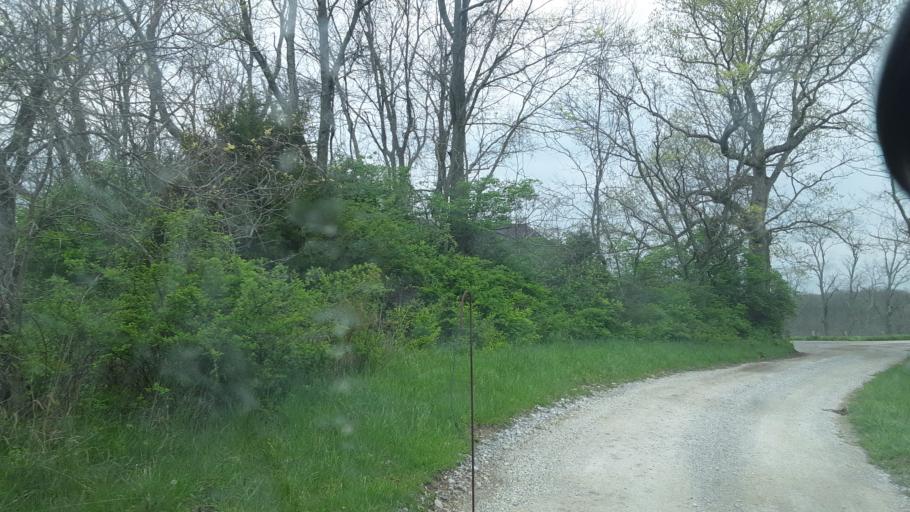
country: US
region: Kentucky
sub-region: Owen County
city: Owenton
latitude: 38.6653
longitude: -84.7816
